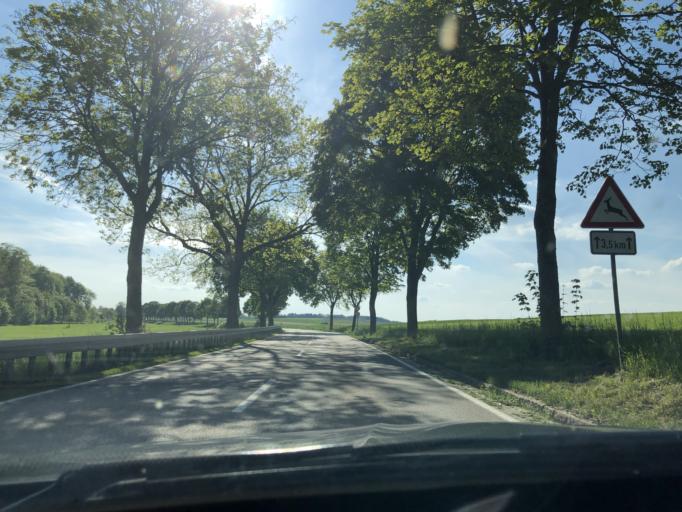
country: DE
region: Bavaria
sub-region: Upper Bavaria
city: Kirchdorf
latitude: 48.4241
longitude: 11.6568
